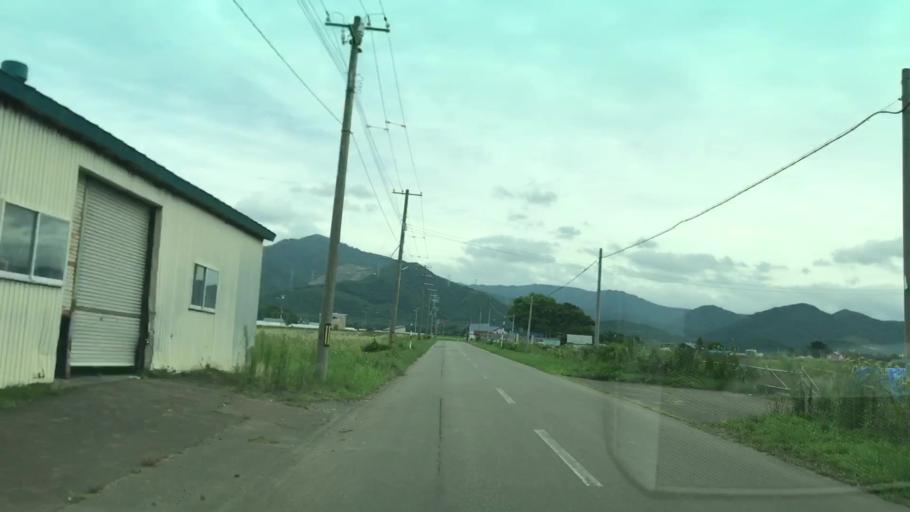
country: JP
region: Hokkaido
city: Iwanai
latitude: 43.0296
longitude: 140.5682
